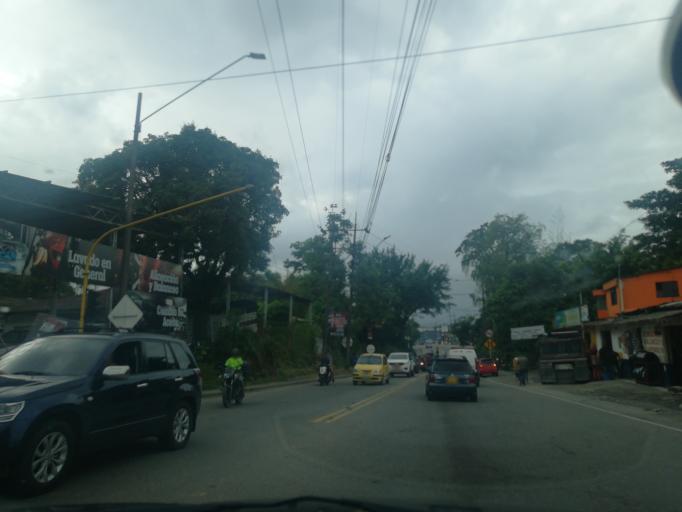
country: CO
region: Meta
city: Acacias
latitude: 3.9900
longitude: -73.7657
